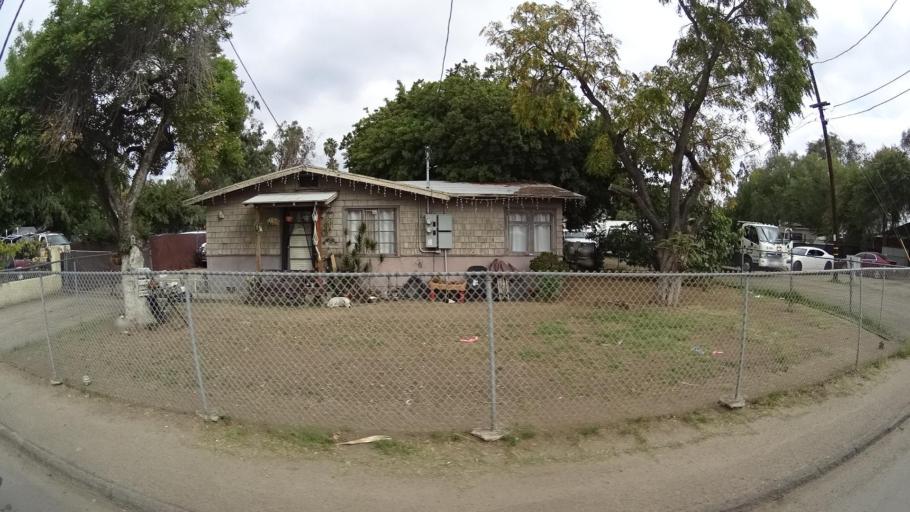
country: US
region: California
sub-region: San Diego County
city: Spring Valley
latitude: 32.7367
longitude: -117.0085
